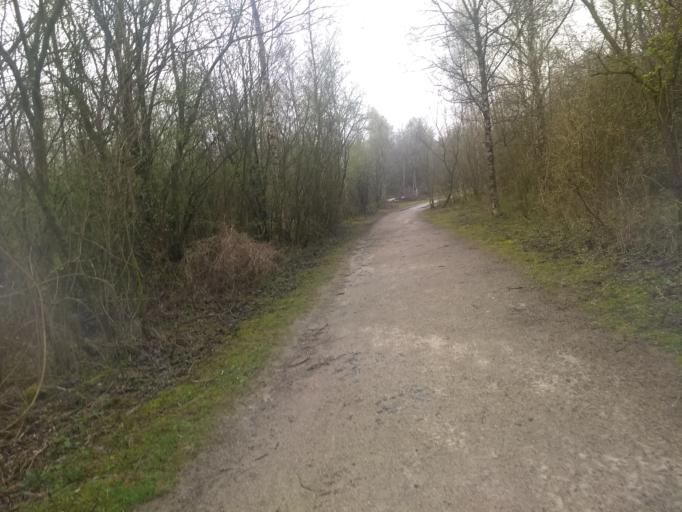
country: FR
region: Nord-Pas-de-Calais
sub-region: Departement du Pas-de-Calais
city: Roeux
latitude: 50.2973
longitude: 2.9207
